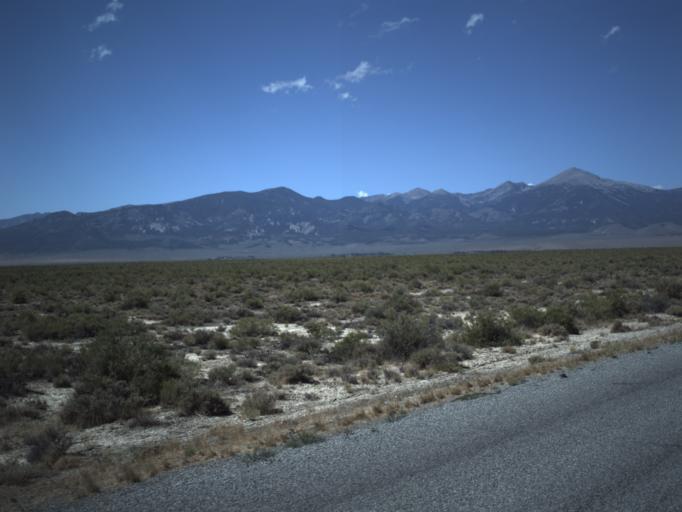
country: US
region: Nevada
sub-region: White Pine County
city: McGill
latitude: 39.0556
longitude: -114.0288
